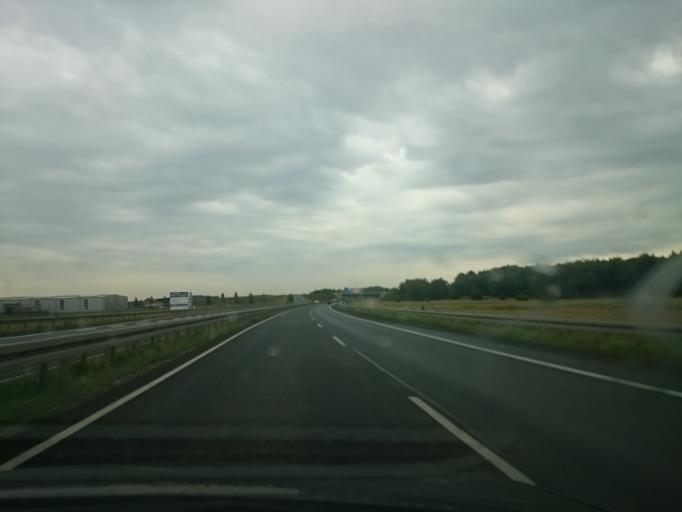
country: DE
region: Brandenburg
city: Leegebruch
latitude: 52.7245
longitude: 13.2169
